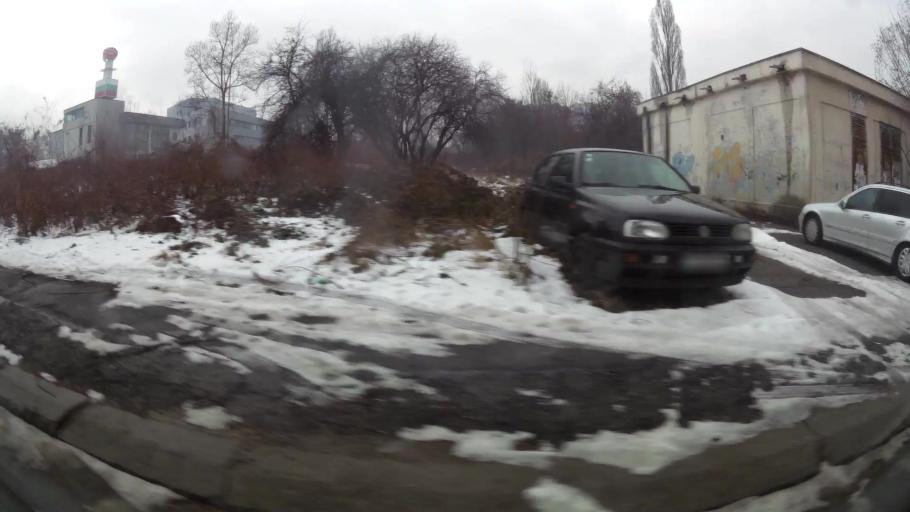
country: BG
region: Sofia-Capital
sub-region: Stolichna Obshtina
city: Sofia
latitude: 42.6819
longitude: 23.2466
